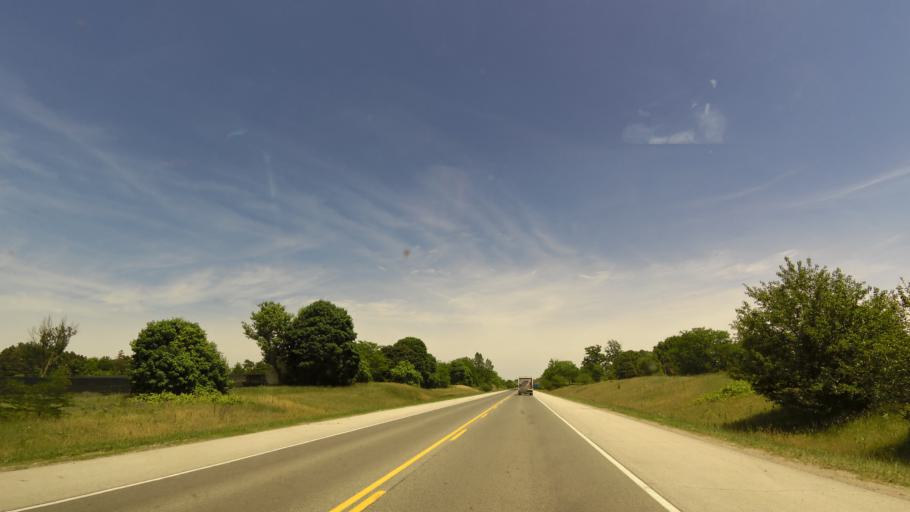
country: CA
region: Ontario
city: Ingersoll
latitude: 42.8519
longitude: -80.7002
